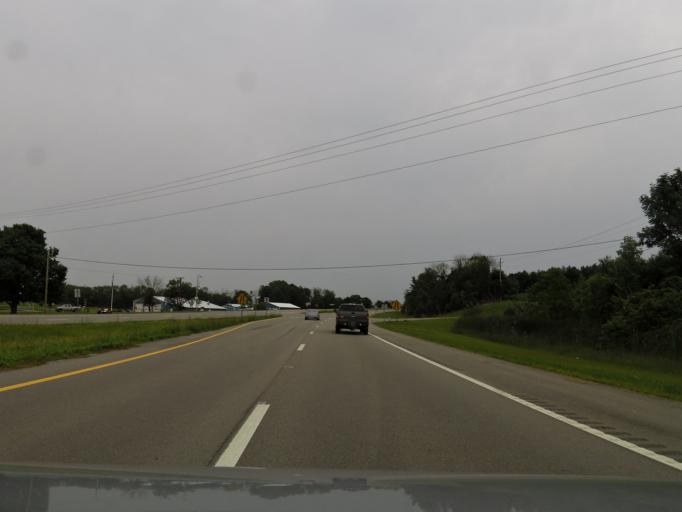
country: US
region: Ohio
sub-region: Warren County
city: Waynesville
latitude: 39.4996
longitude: -84.0018
